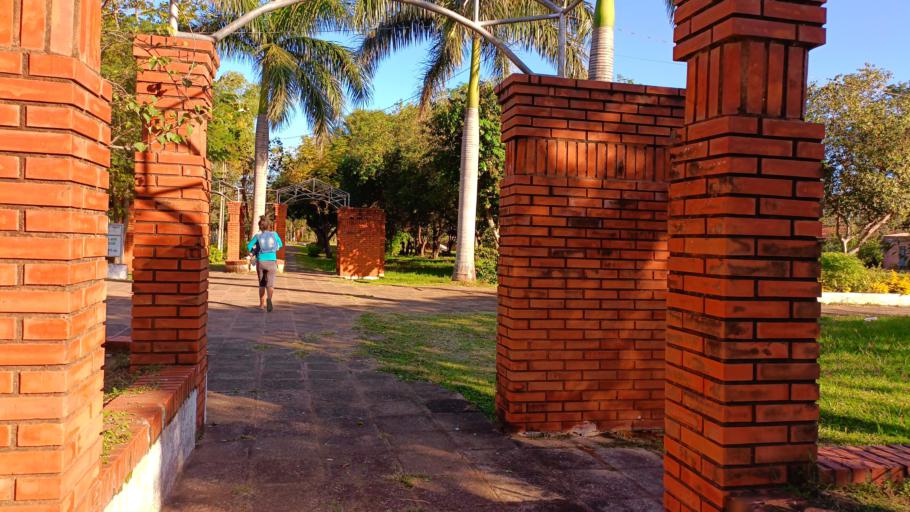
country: PY
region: Itapua
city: Carmen del Parana
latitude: -27.1623
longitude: -56.2403
